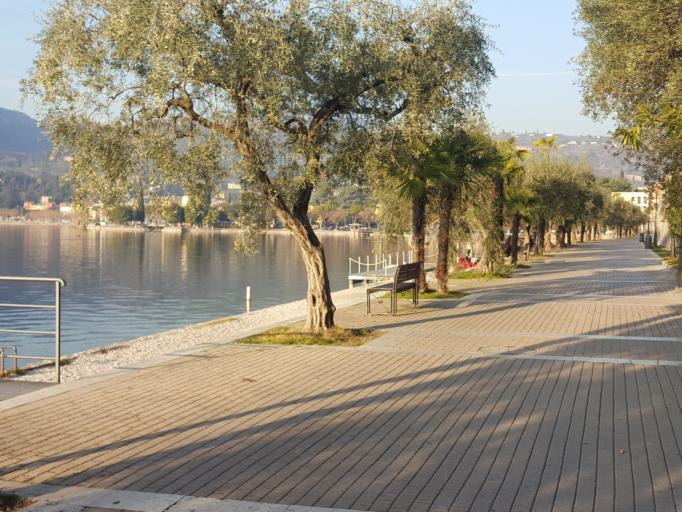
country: IT
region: Veneto
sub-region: Provincia di Verona
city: Garda
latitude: 45.5696
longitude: 10.7087
